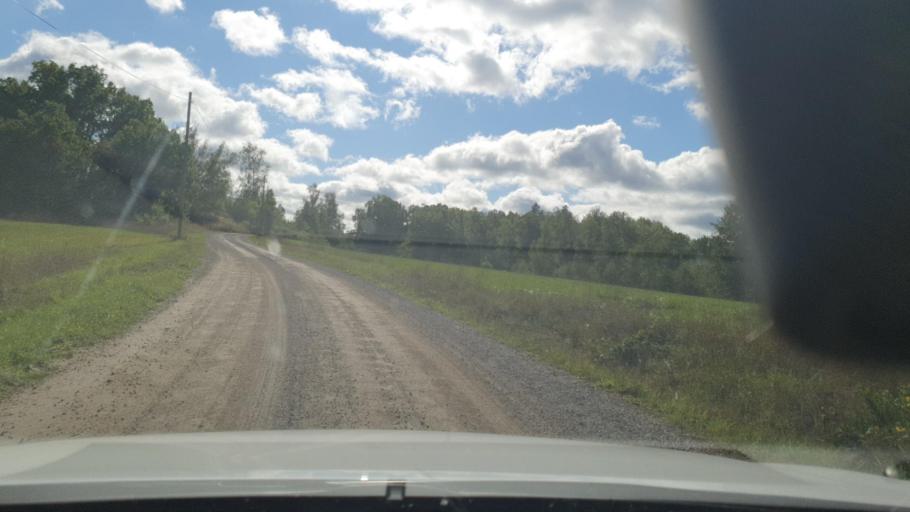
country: SE
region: Kalmar
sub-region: Vasterviks Kommun
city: Ankarsrum
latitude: 57.7054
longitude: 16.4525
